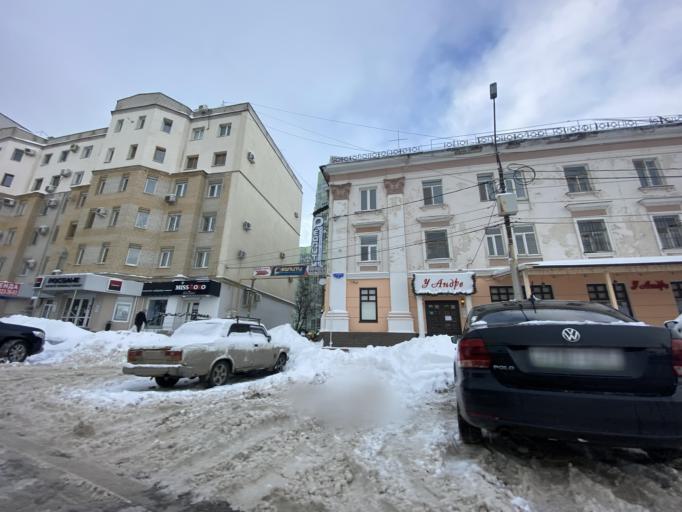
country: RU
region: Saratov
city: Engel's
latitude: 51.5034
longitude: 46.1177
